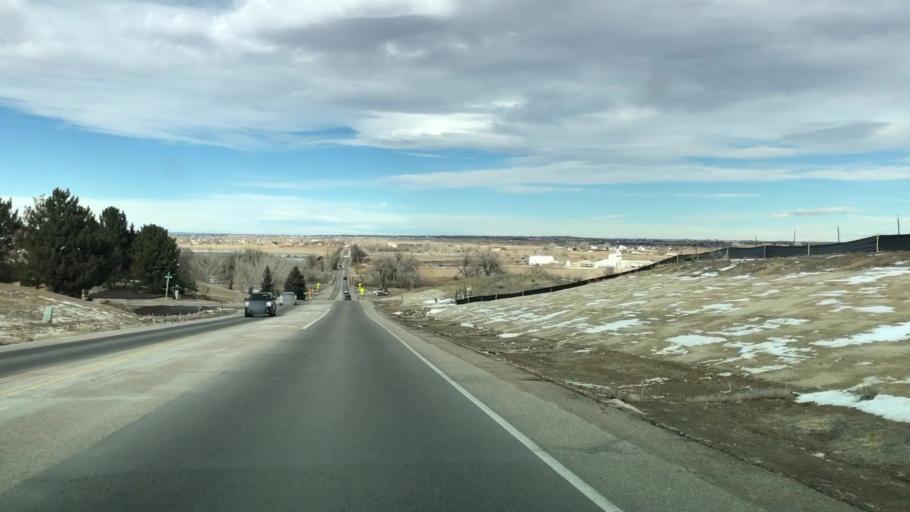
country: US
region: Colorado
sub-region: Weld County
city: Windsor
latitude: 40.4692
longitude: -104.9441
